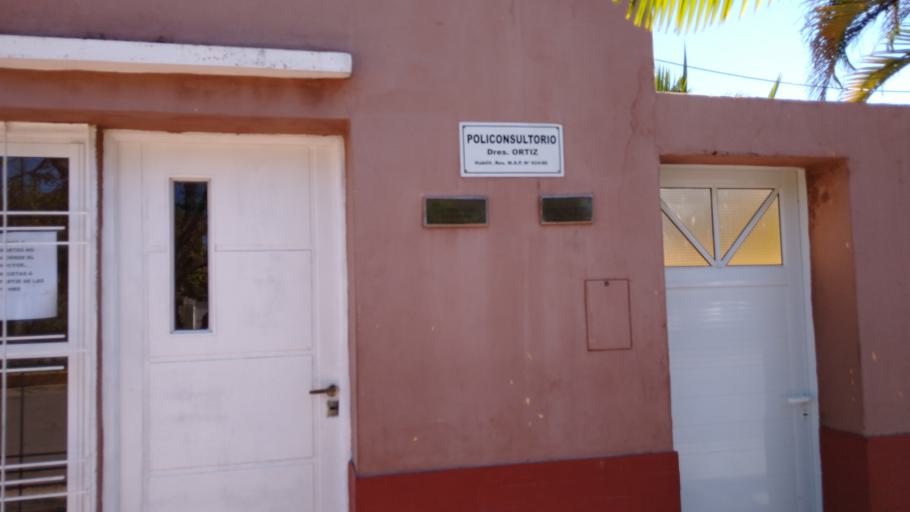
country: AR
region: Corrientes
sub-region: Departamento de San Miguel
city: San Miguel
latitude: -27.9954
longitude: -57.5925
